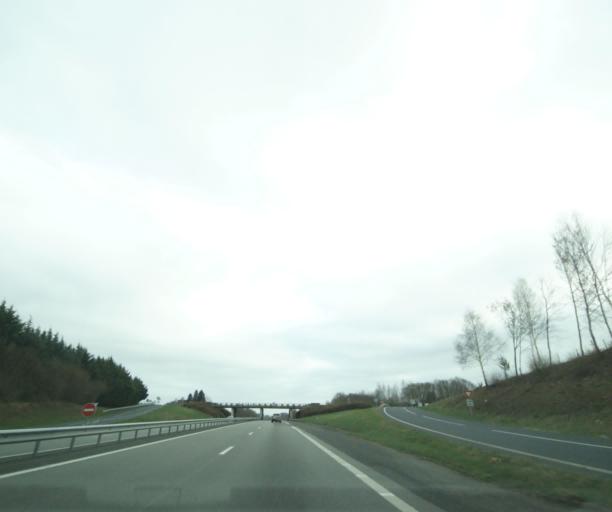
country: FR
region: Limousin
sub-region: Departement de la Correze
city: Vigeois
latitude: 45.3210
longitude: 1.5730
